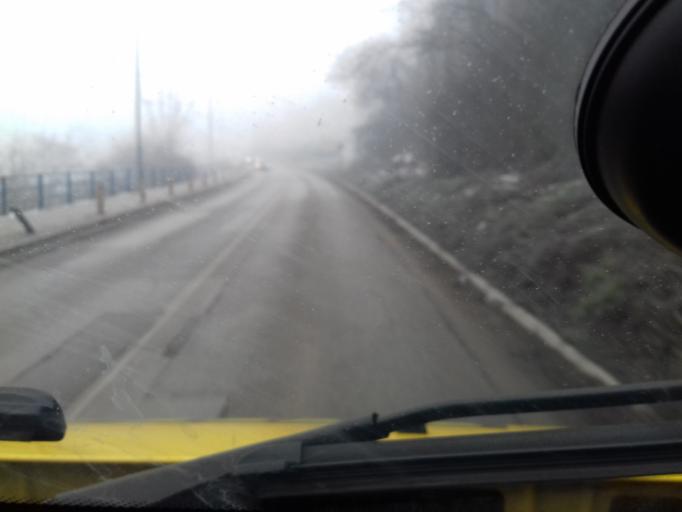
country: BA
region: Federation of Bosnia and Herzegovina
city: Visoko
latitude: 43.9969
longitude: 18.1663
